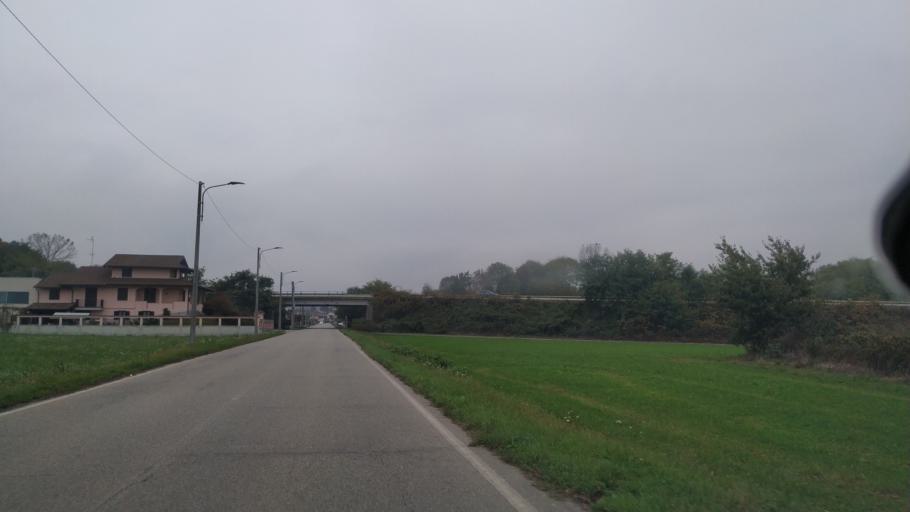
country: IT
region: Piedmont
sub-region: Provincia di Biella
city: Cerreto Castello
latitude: 45.5518
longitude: 8.1735
